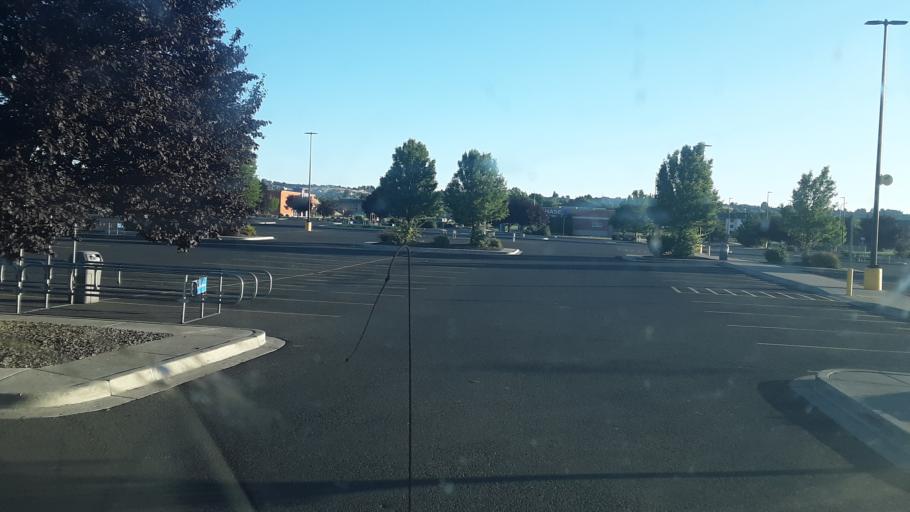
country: US
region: Washington
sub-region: Yakima County
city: West Valley
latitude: 46.5837
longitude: -120.5967
